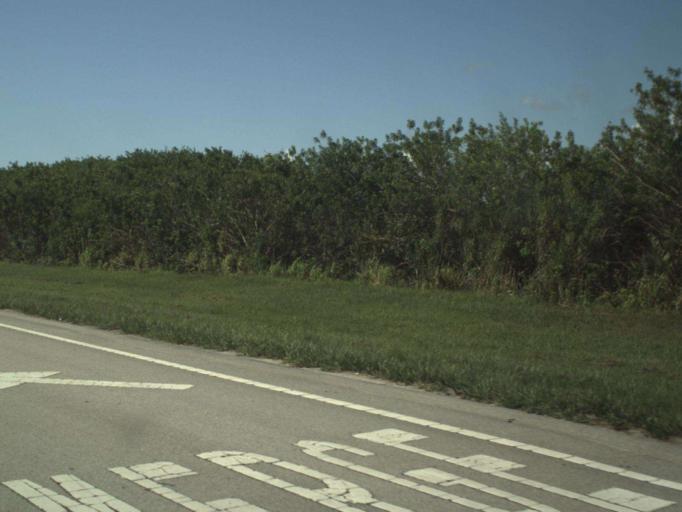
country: US
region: Florida
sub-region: Indian River County
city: Gifford
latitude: 27.6669
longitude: -80.3933
